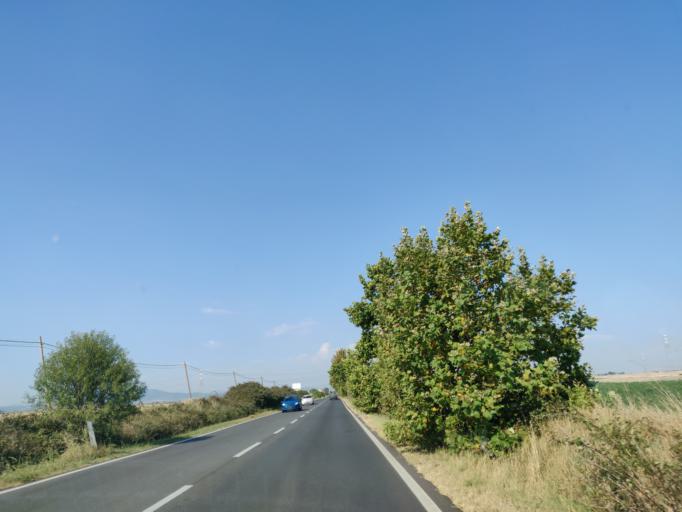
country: IT
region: Latium
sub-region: Provincia di Viterbo
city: Montalto di Castro
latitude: 42.3544
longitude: 11.6360
